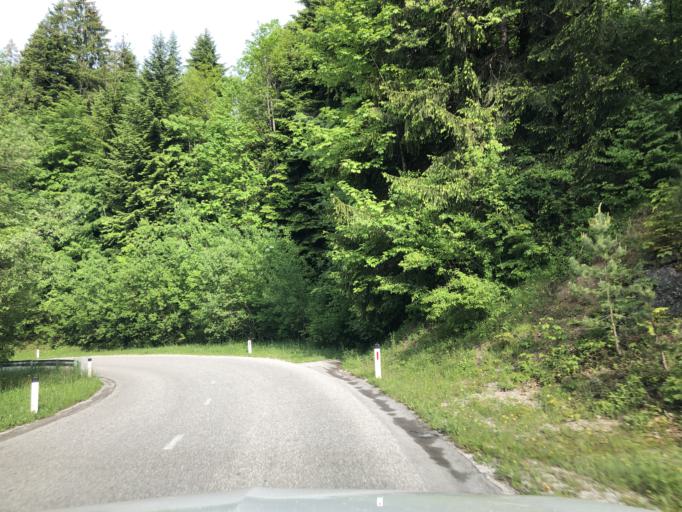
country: SI
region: Velike Lasce
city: Velike Lasce
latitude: 45.8102
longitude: 14.6220
